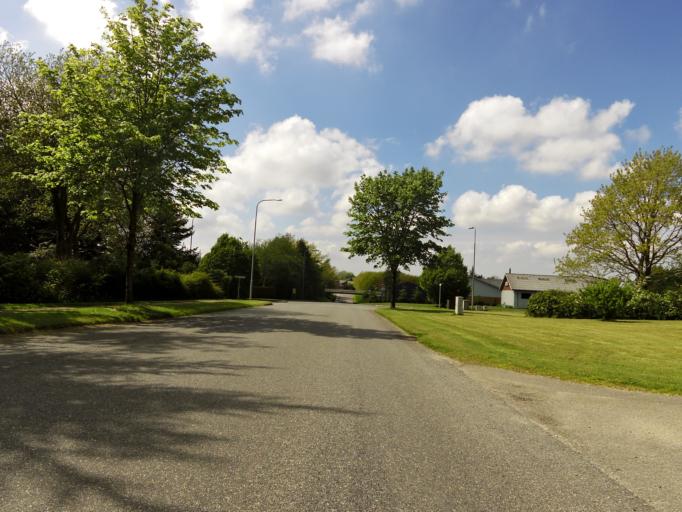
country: DK
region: South Denmark
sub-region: Tonder Kommune
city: Toftlund
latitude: 55.1904
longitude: 9.0777
